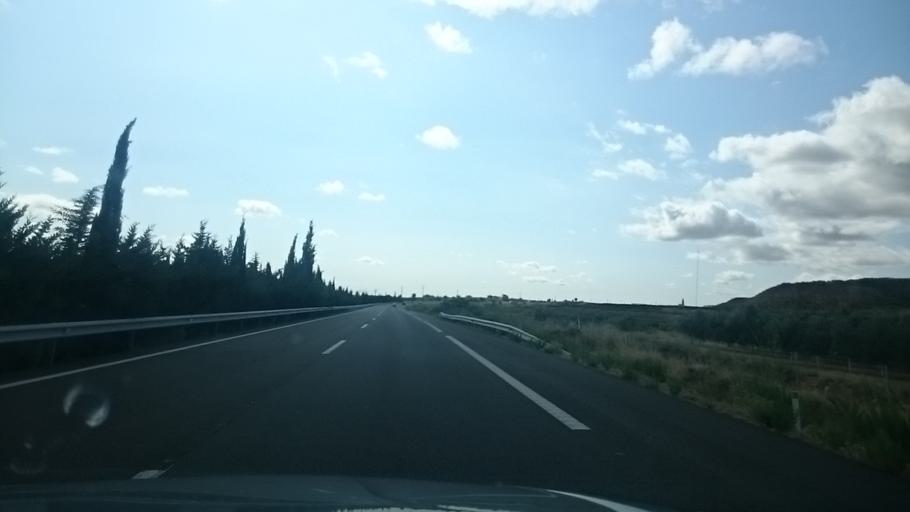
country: ES
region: La Rioja
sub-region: Provincia de La Rioja
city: Aldeanueva de Ebro
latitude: 42.2505
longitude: -1.9113
